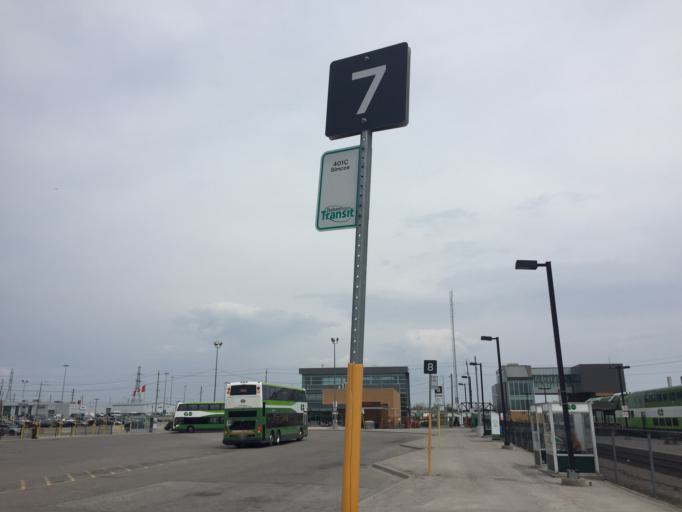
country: CA
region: Ontario
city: Oshawa
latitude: 43.8705
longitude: -78.8865
